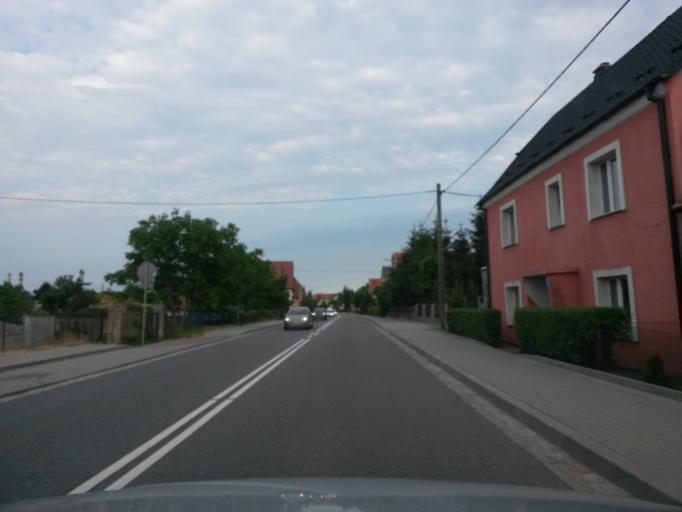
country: PL
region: Lower Silesian Voivodeship
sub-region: Powiat sredzki
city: Udanin
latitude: 50.9872
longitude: 16.4257
